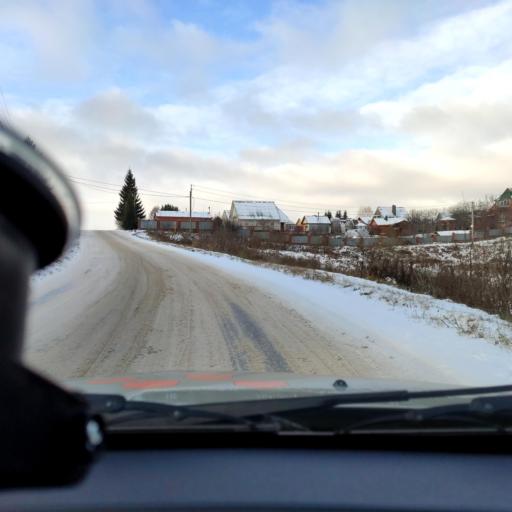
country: RU
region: Bashkortostan
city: Avdon
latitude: 54.7834
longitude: 55.7355
